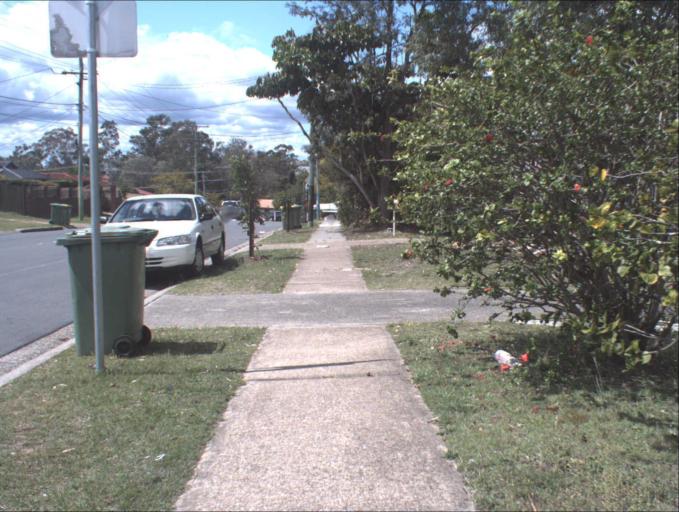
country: AU
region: Queensland
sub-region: Logan
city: Park Ridge South
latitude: -27.6685
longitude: 153.0265
